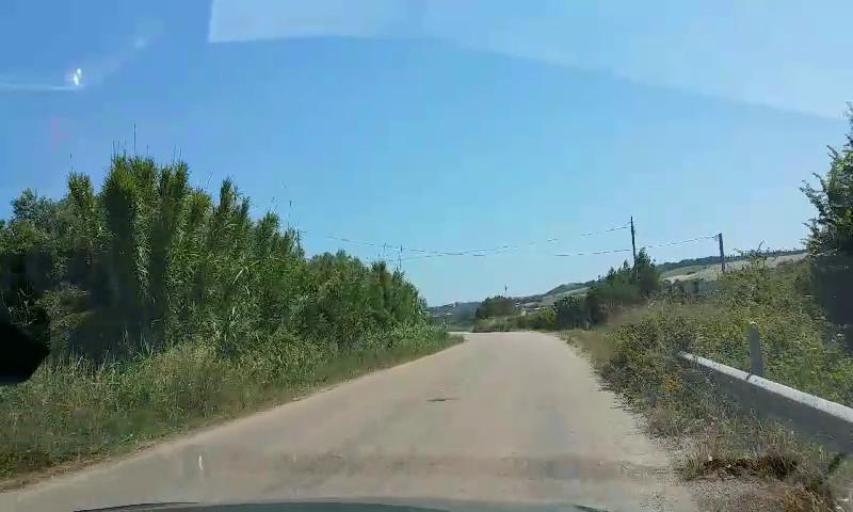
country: IT
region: Molise
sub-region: Provincia di Campobasso
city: San Giacomo degli Schiavoni
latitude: 41.9876
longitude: 14.9393
